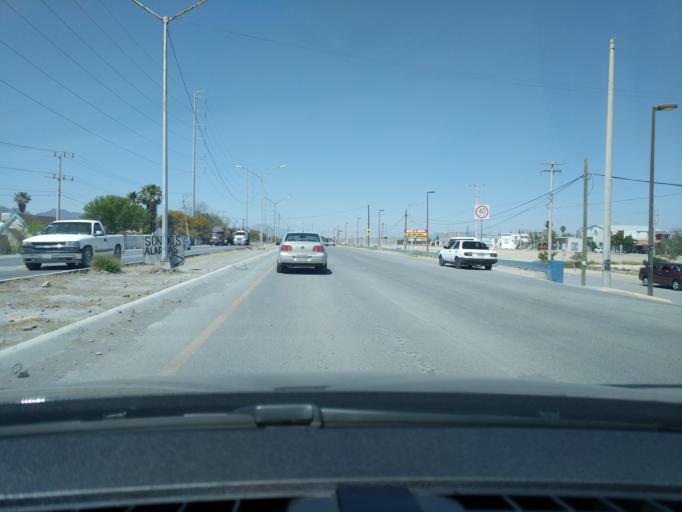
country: MX
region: Nuevo Leon
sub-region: Salinas Victoria
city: Emiliano Zapata
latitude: 25.9139
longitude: -100.2681
